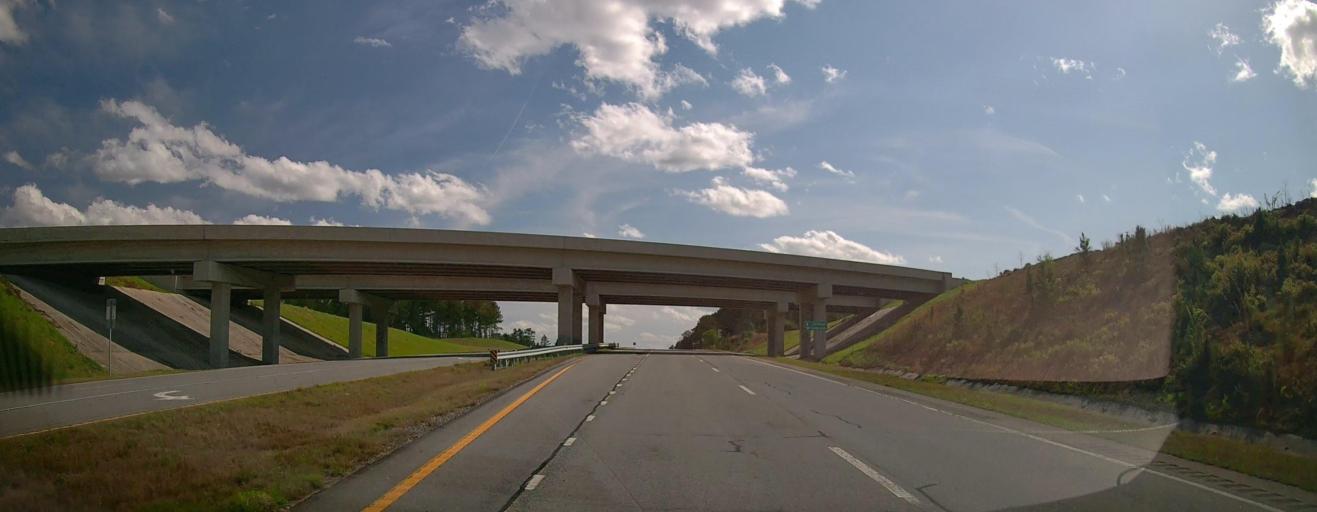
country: US
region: Georgia
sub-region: Baldwin County
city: Hardwick
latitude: 32.9800
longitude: -83.2138
